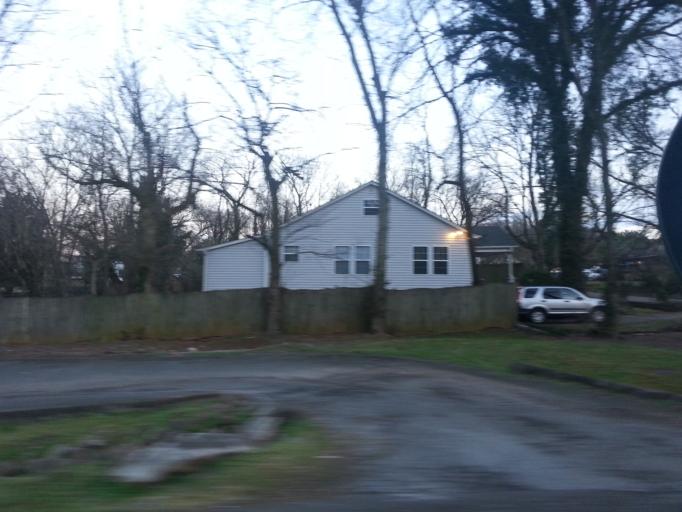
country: US
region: Tennessee
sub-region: Knox County
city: Knoxville
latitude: 35.9483
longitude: -83.8891
